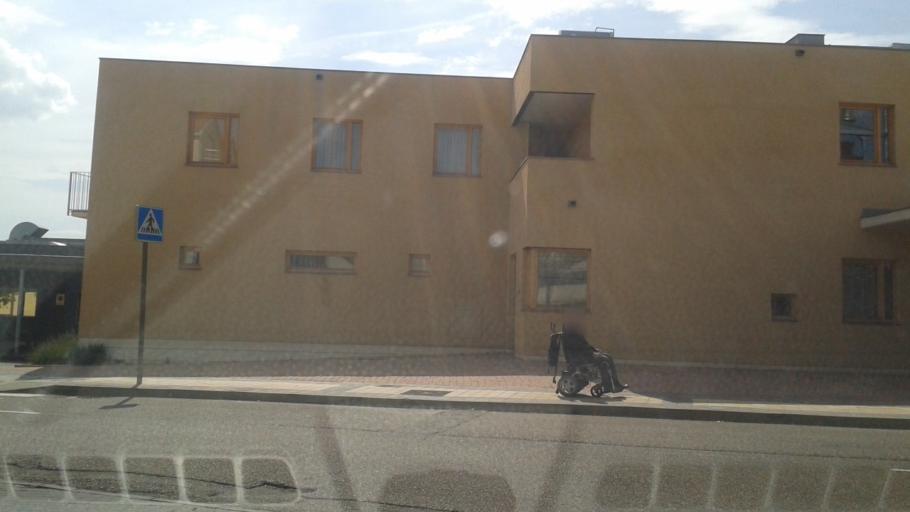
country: ES
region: Castille and Leon
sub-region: Provincia de Valladolid
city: Arroyo
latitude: 41.6265
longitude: -4.7746
